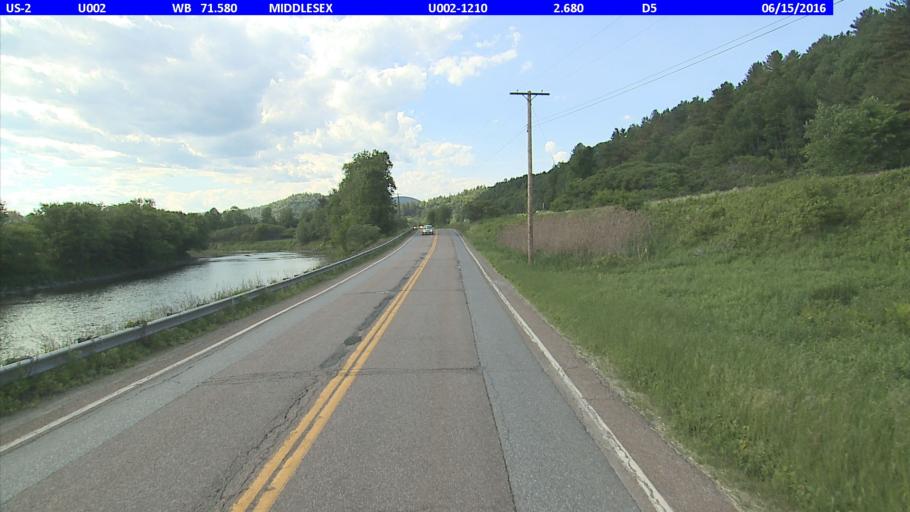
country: US
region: Vermont
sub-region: Washington County
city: Montpelier
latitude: 44.2808
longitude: -72.6602
